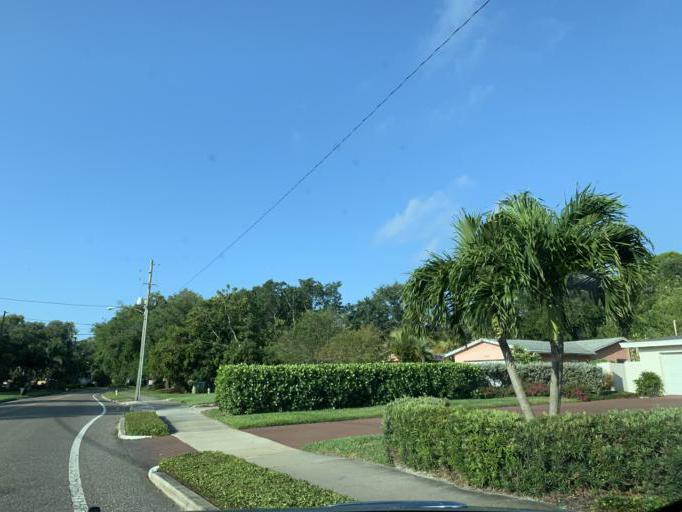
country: US
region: Florida
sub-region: Pinellas County
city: Gandy
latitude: 27.7974
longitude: -82.6104
